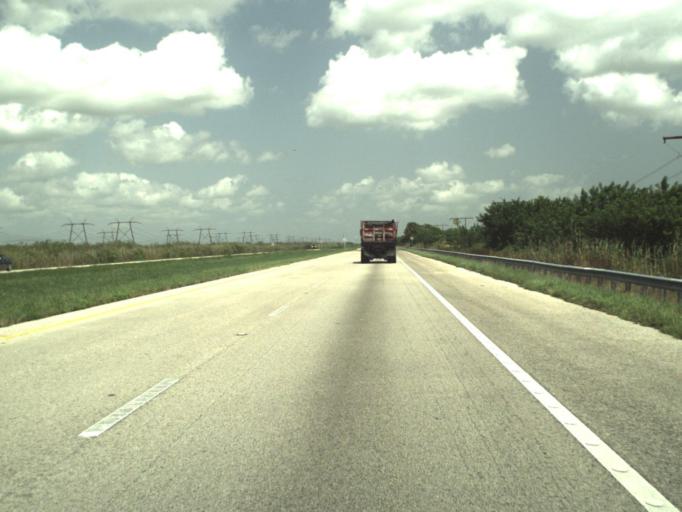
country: US
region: Florida
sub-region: Broward County
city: Weston
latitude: 26.2674
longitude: -80.4855
